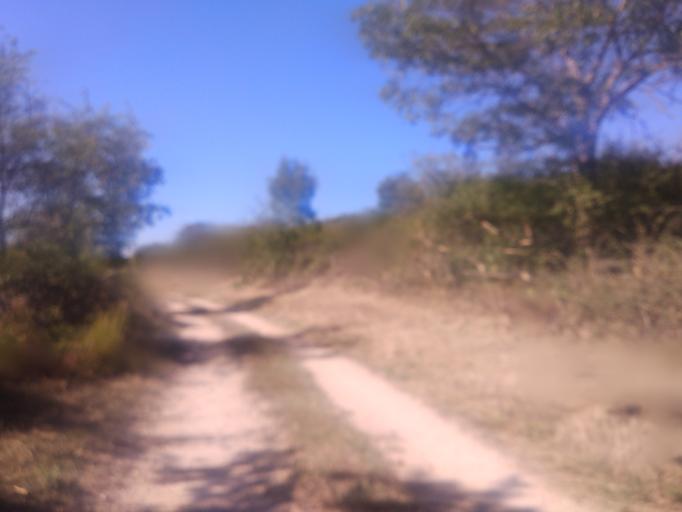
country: FR
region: Rhone-Alpes
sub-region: Departement de l'Ardeche
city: Sarras
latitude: 45.1946
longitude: 4.7595
